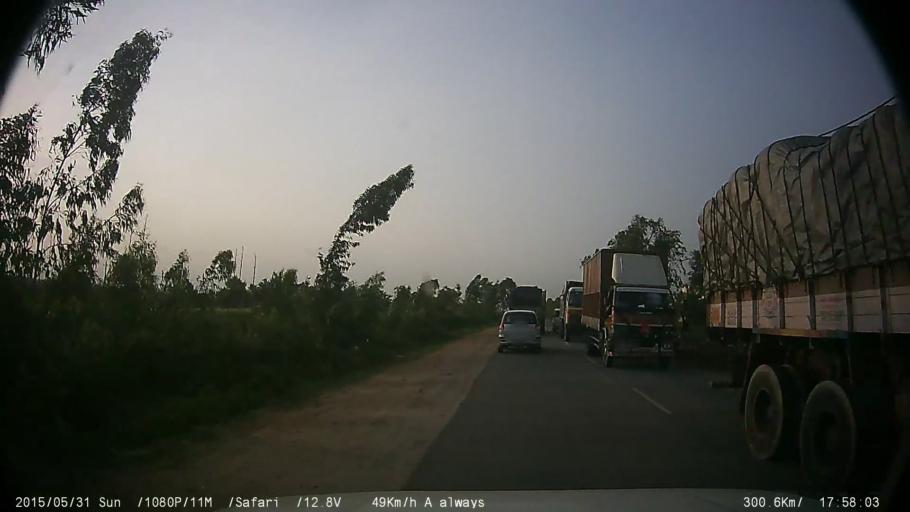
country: IN
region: Karnataka
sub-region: Mysore
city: Nanjangud
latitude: 12.0063
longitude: 76.6693
